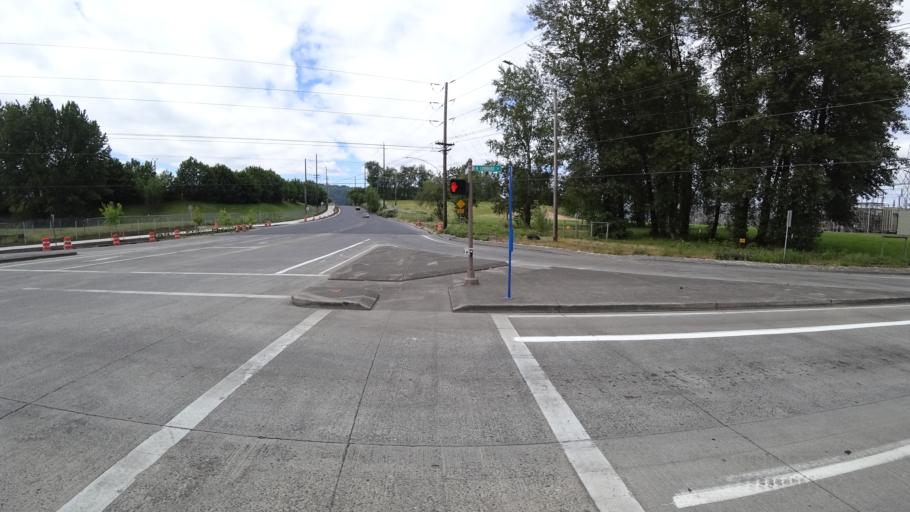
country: US
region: Oregon
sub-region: Washington County
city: West Haven
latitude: 45.6127
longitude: -122.7629
